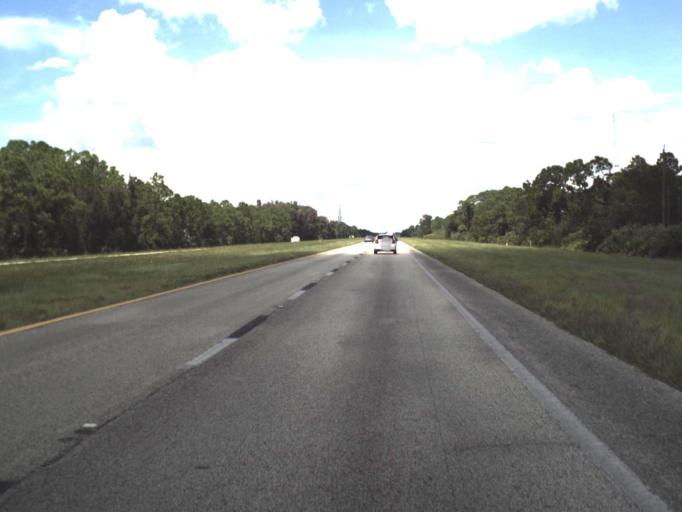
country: US
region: Florida
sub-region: Lee County
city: Burnt Store Marina
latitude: 26.8229
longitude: -81.9651
